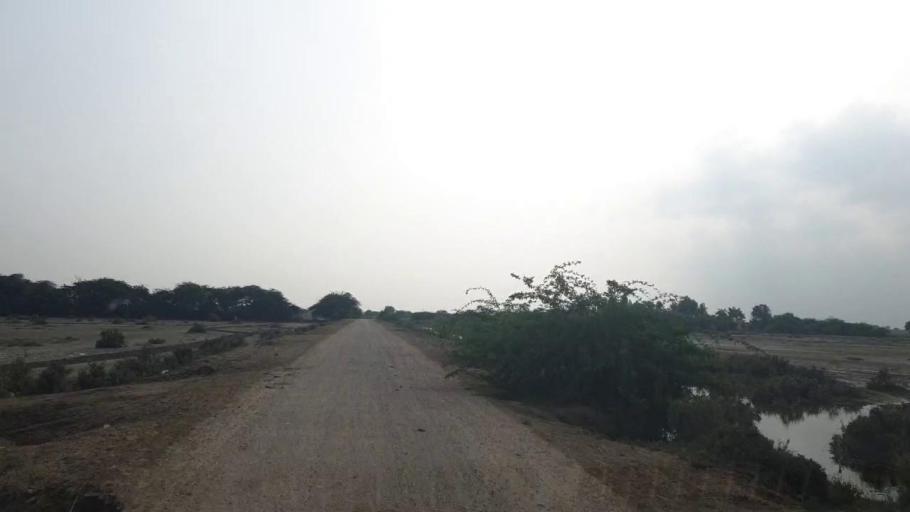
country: PK
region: Sindh
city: Badin
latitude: 24.6277
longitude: 68.6916
